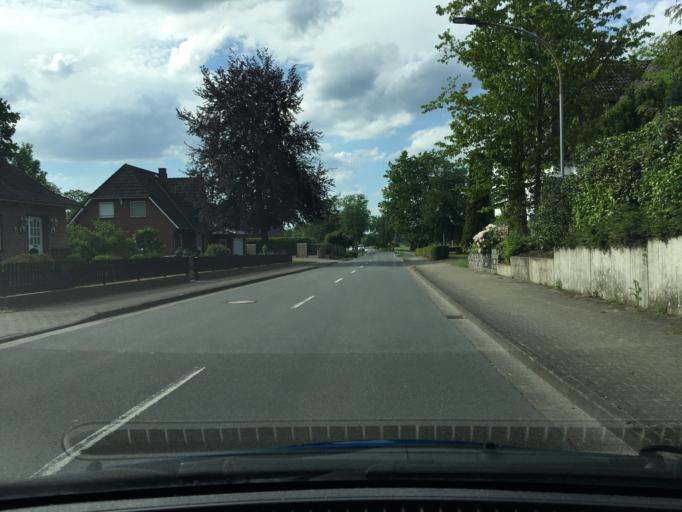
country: DE
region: Lower Saxony
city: Welle
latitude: 53.2413
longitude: 9.7995
